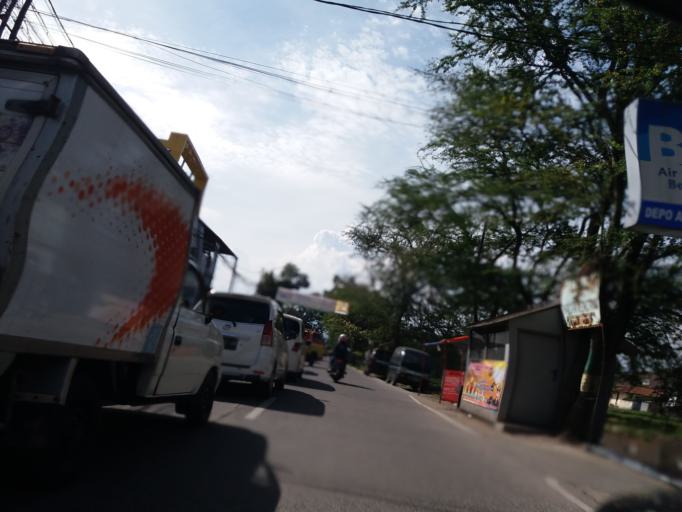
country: ID
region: West Java
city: Bandung
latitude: -6.9399
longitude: 107.6128
